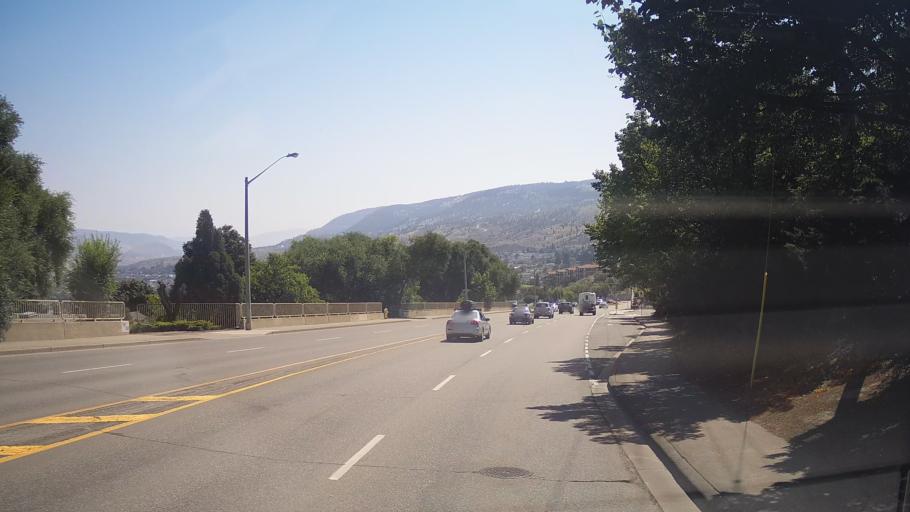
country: CA
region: British Columbia
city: Kamloops
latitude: 50.6738
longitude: -120.3484
